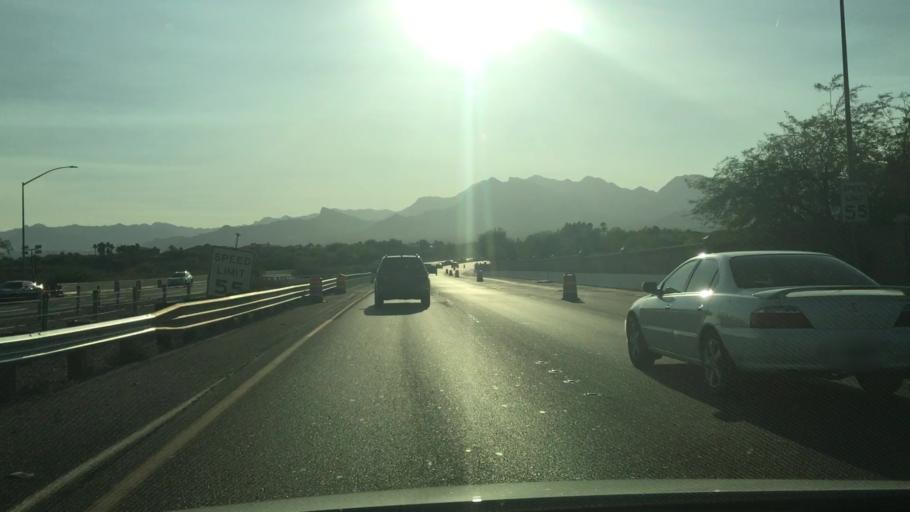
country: US
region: Nevada
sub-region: Clark County
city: Summerlin South
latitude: 36.1782
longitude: -115.2905
